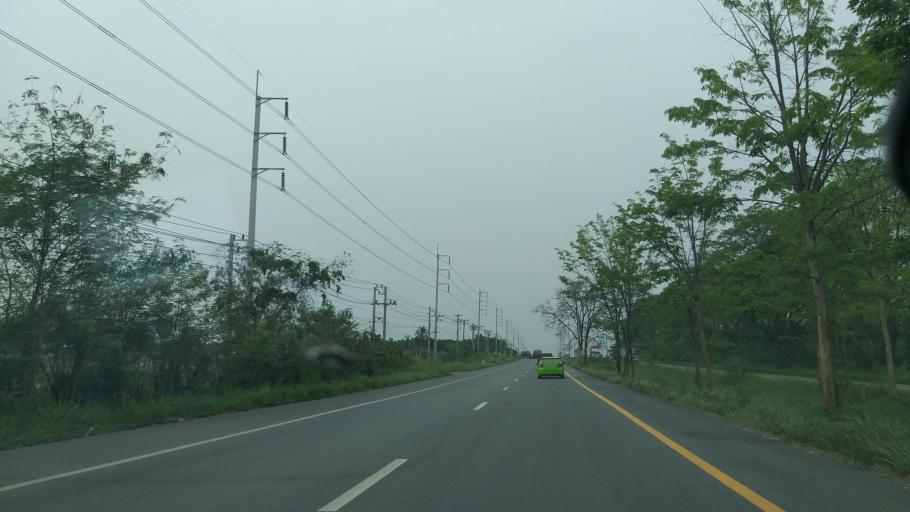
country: TH
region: Chon Buri
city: Ko Chan
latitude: 13.4572
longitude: 101.2838
